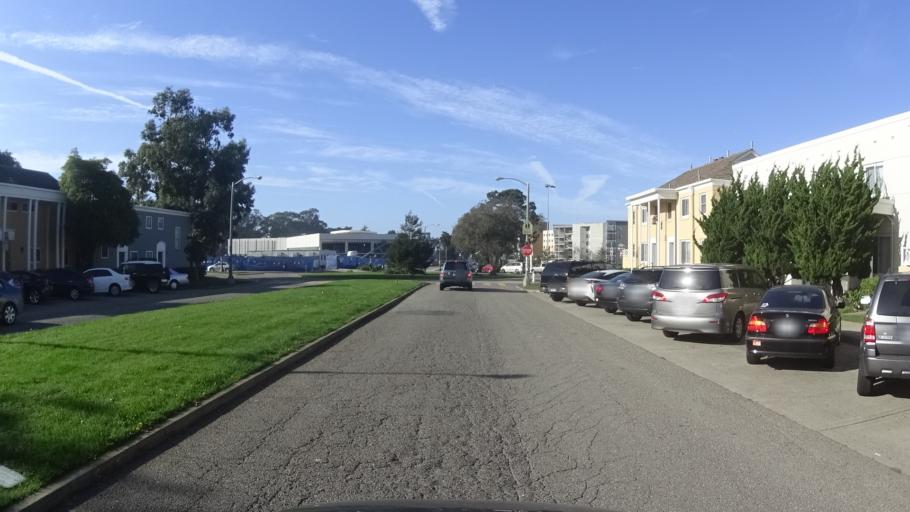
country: US
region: California
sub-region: San Mateo County
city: Daly City
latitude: 37.7214
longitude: -122.4817
